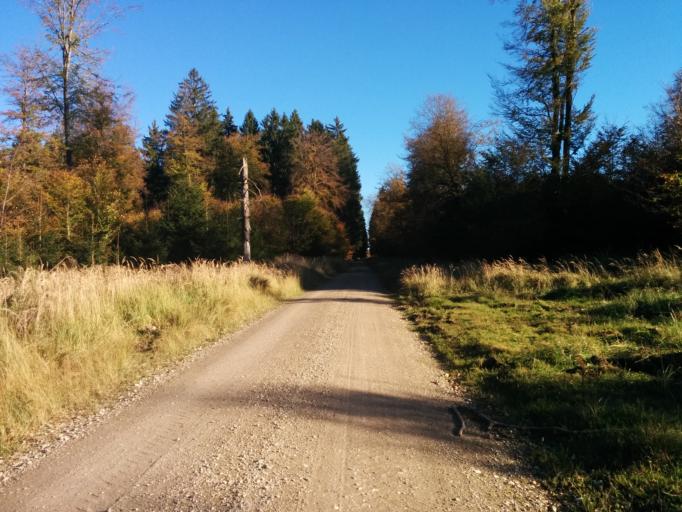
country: DE
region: Bavaria
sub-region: Upper Bavaria
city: Schaftlarn
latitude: 48.0174
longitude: 11.4550
